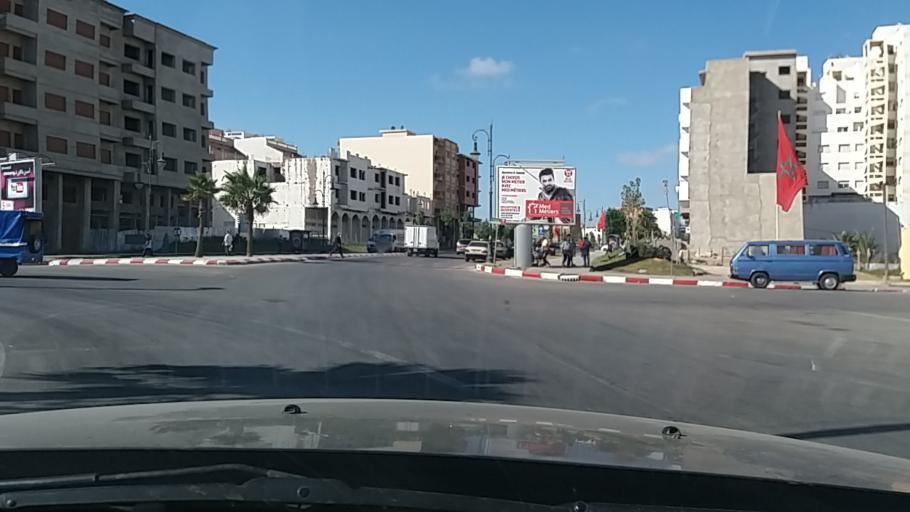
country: MA
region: Tanger-Tetouan
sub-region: Tanger-Assilah
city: Boukhalef
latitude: 35.7534
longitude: -5.8512
